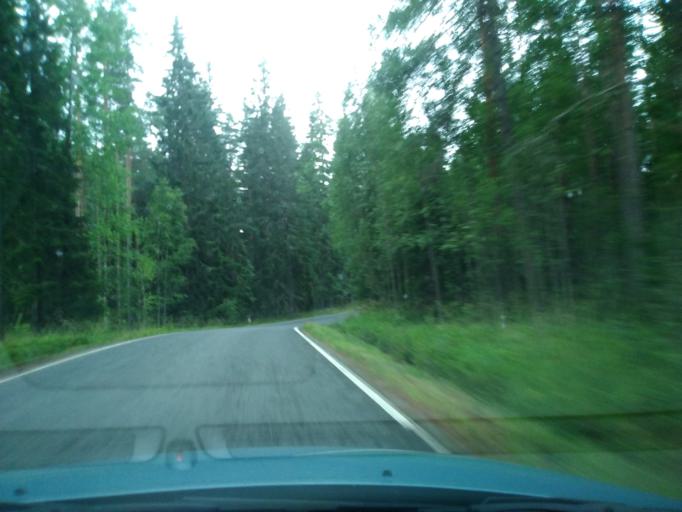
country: FI
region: Uusimaa
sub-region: Helsinki
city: Kaerkoelae
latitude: 60.7834
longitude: 24.0791
